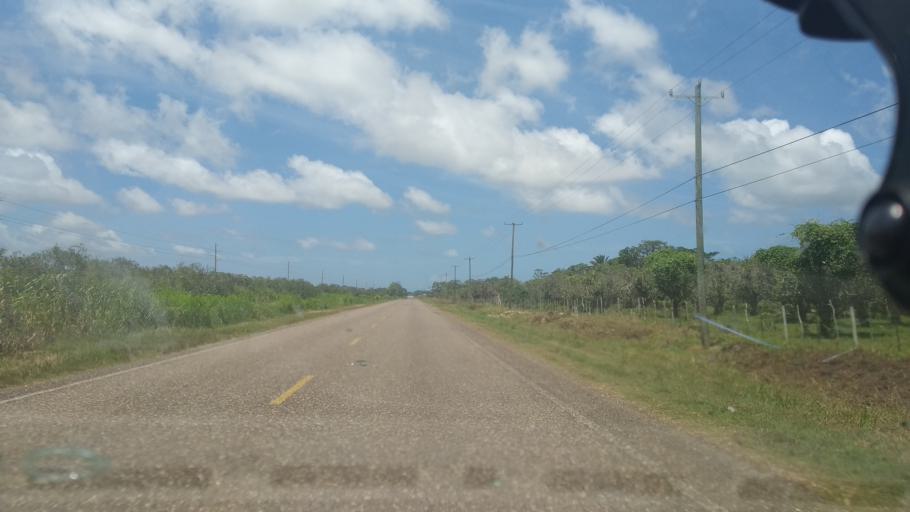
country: BZ
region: Stann Creek
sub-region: Dangriga
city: Dangriga
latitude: 16.8273
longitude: -88.3687
